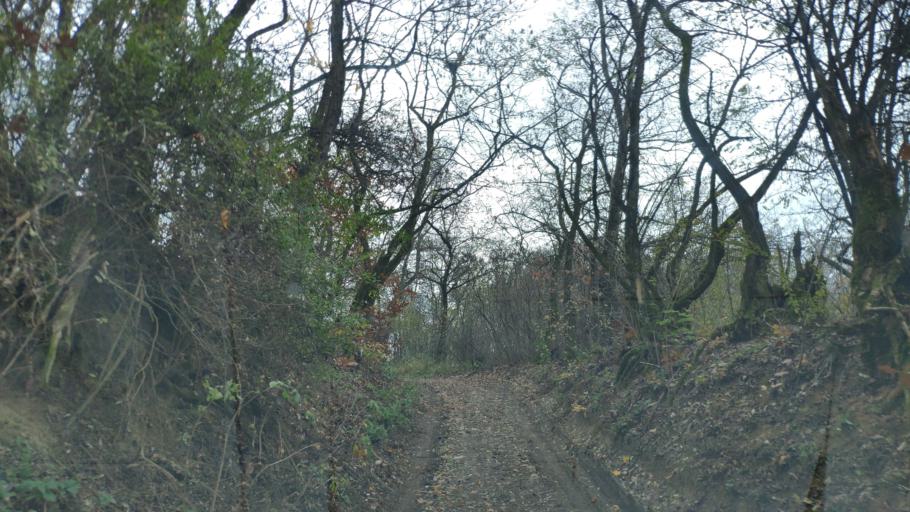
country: SK
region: Kosicky
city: Kosice
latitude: 48.6955
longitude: 21.2928
